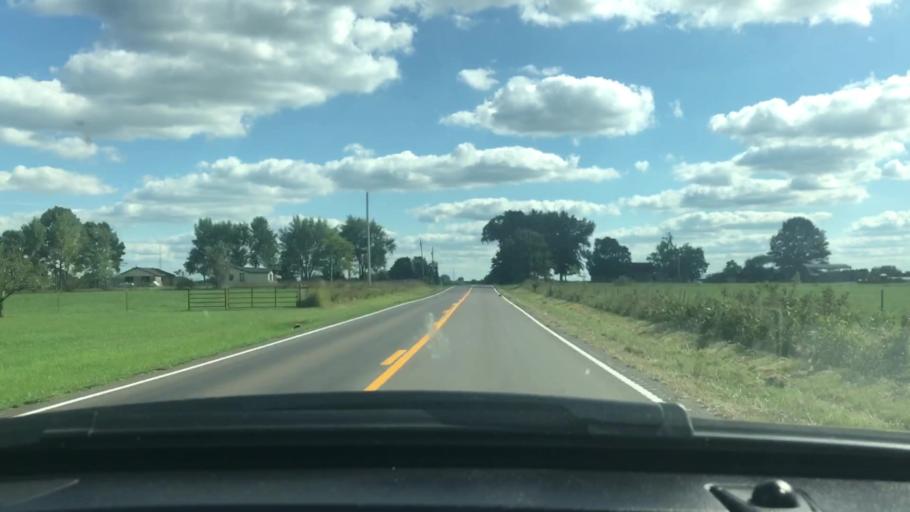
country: US
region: Missouri
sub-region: Wright County
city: Mountain Grove
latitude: 37.2641
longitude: -92.3081
